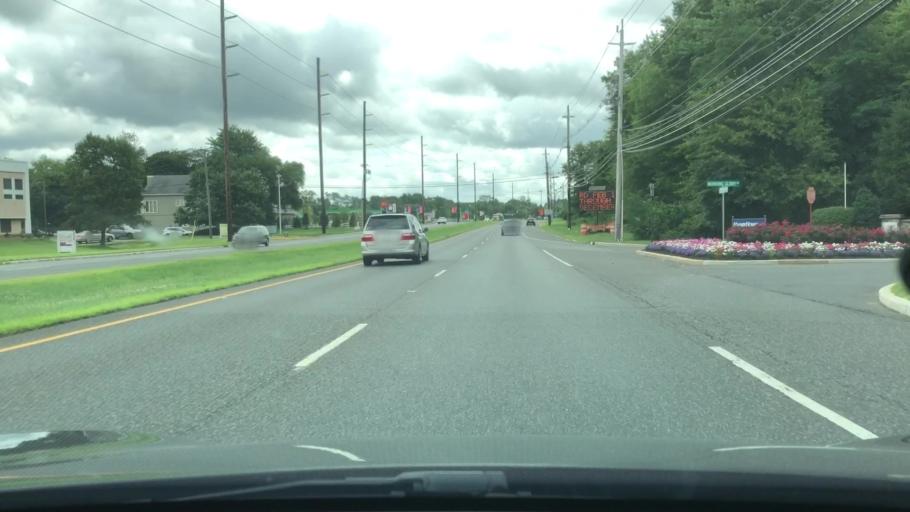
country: US
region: New Jersey
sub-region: Mercer County
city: Twin Rivers
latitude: 40.2675
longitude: -74.4756
